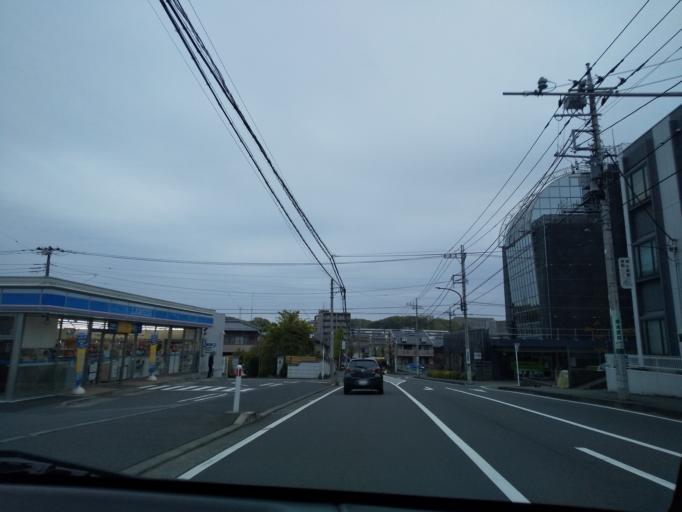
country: JP
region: Tokyo
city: Hachioji
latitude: 35.5978
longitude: 139.3467
